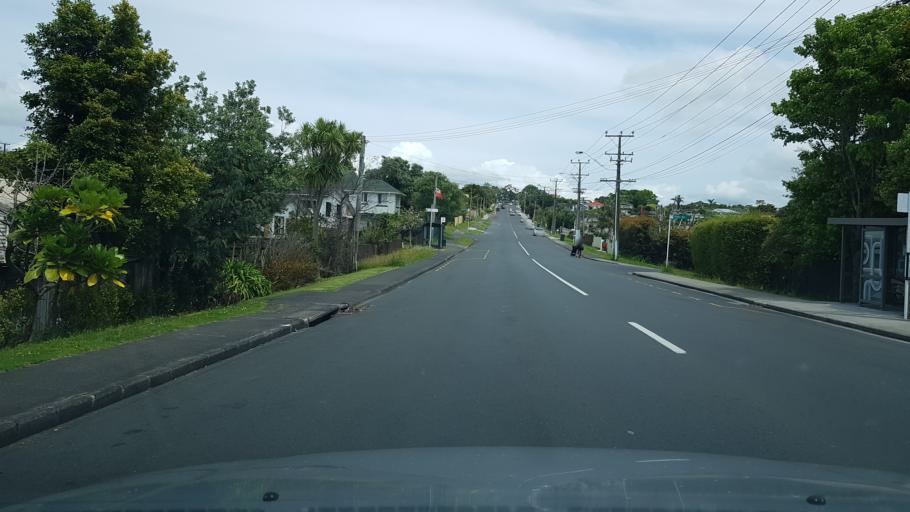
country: NZ
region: Auckland
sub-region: Auckland
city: North Shore
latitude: -36.8023
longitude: 174.7310
